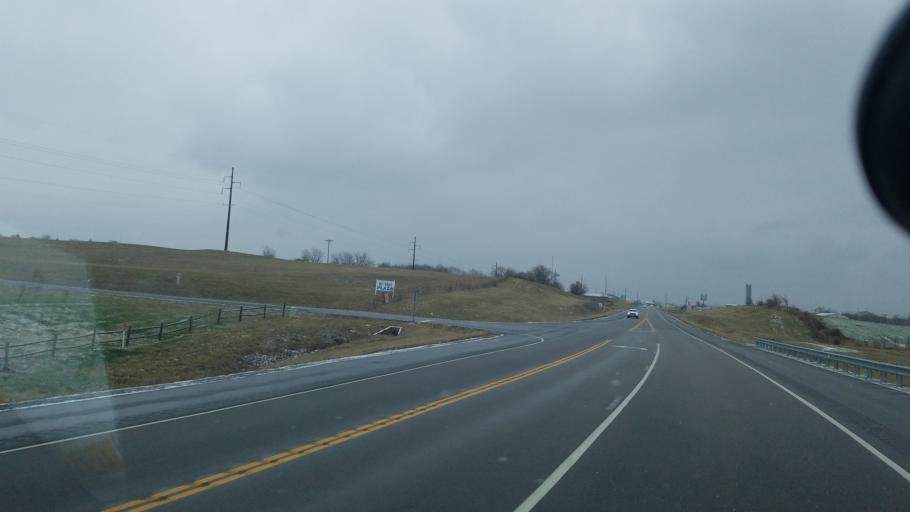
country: US
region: Kentucky
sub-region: Fleming County
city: Flemingsburg
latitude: 38.4158
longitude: -83.7510
